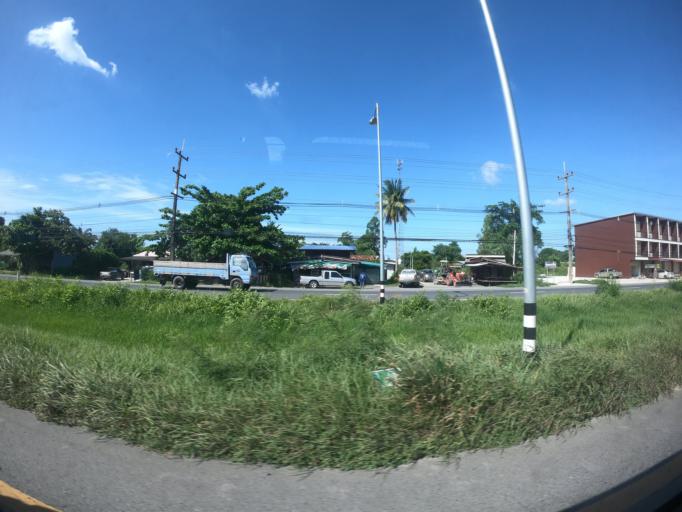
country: TH
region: Nakhon Nayok
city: Ban Na
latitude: 14.2532
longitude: 101.0936
